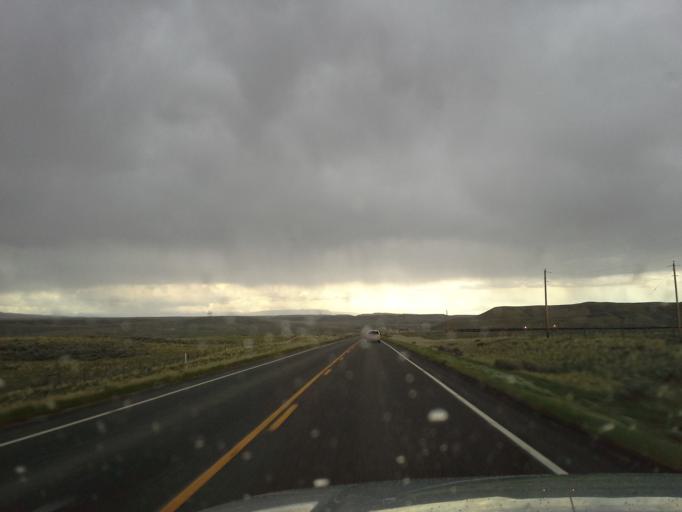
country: US
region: Wyoming
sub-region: Park County
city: Powell
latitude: 45.0690
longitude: -108.6779
